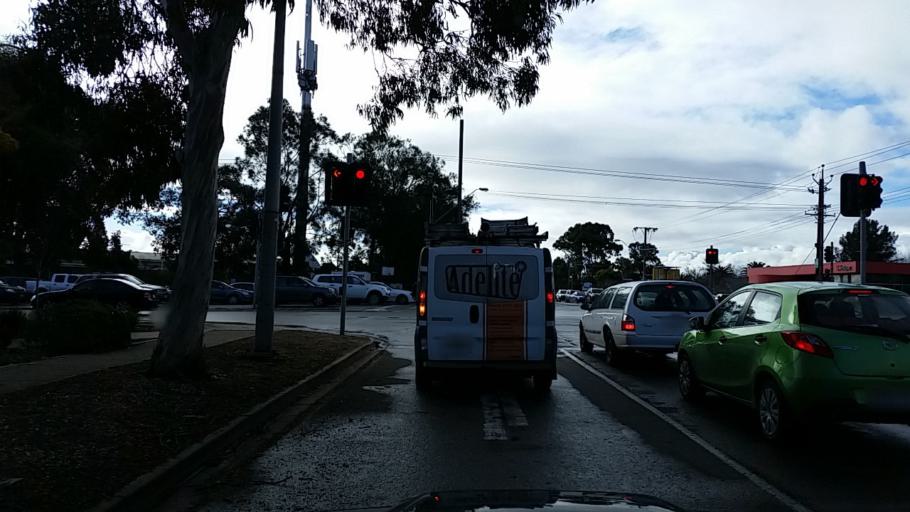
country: AU
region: South Australia
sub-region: Onkaparinga
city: Reynella
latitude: -35.1056
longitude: 138.5220
